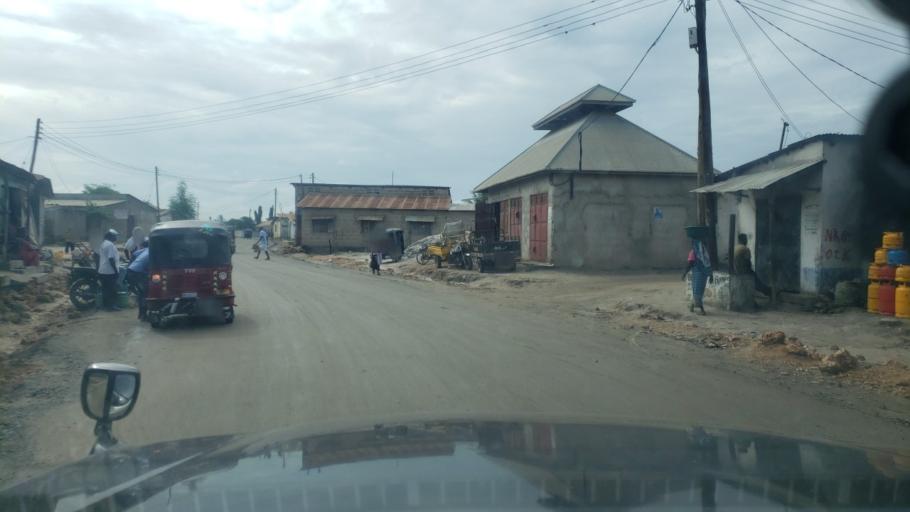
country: TZ
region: Pwani
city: Vikindu
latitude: -6.9265
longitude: 39.2525
